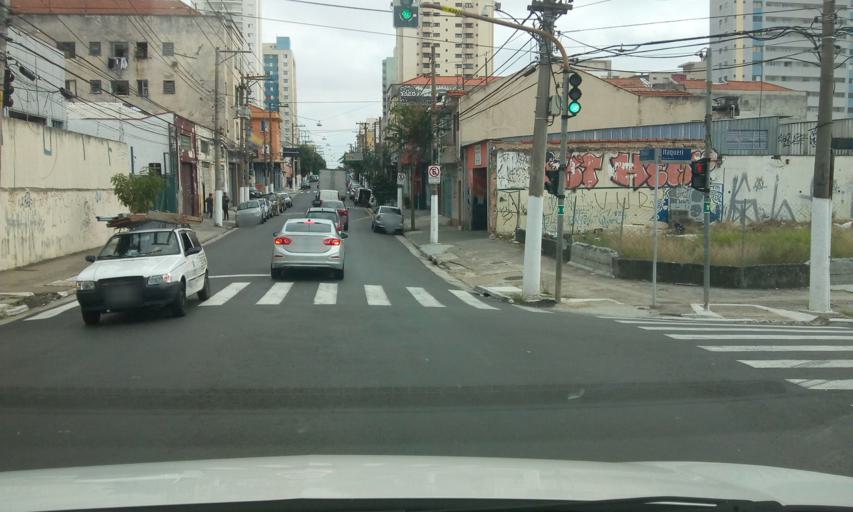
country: BR
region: Sao Paulo
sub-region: Sao Paulo
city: Sao Paulo
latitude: -23.5588
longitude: -46.5896
